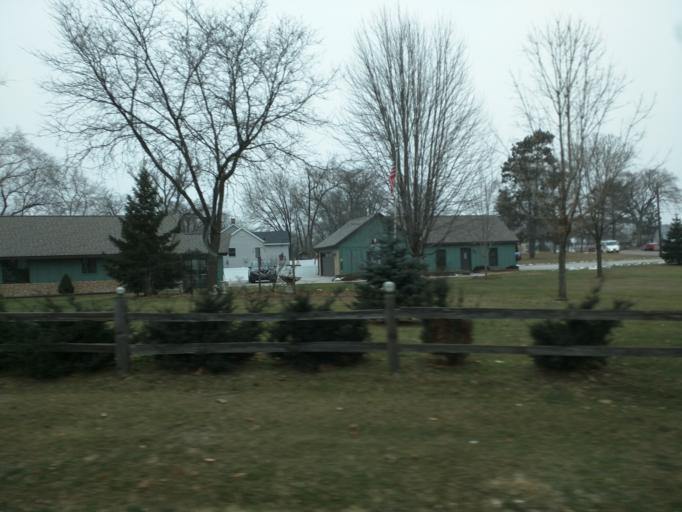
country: US
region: Wisconsin
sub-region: La Crosse County
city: French Island
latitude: 43.8456
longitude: -91.2643
